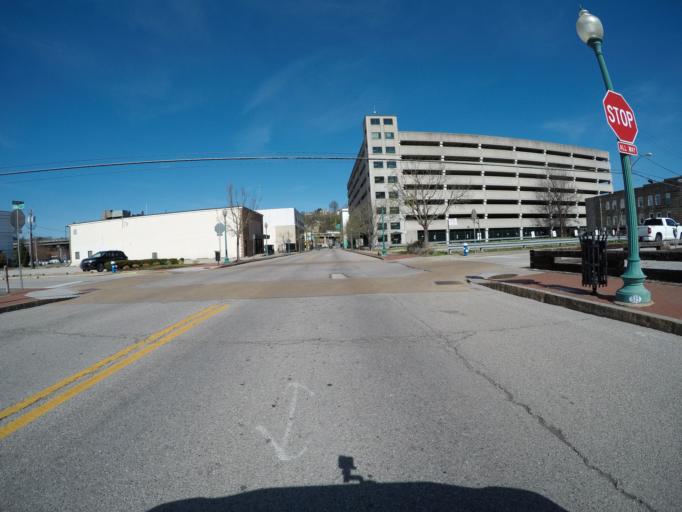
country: US
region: West Virginia
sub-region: Kanawha County
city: Charleston
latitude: 38.3520
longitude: -81.6307
